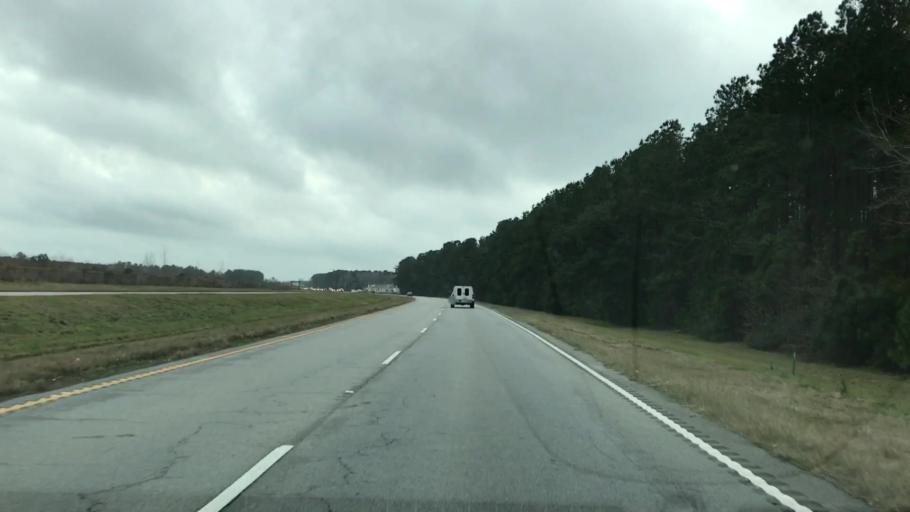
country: US
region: South Carolina
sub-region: Berkeley County
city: Moncks Corner
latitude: 33.1588
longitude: -80.0324
